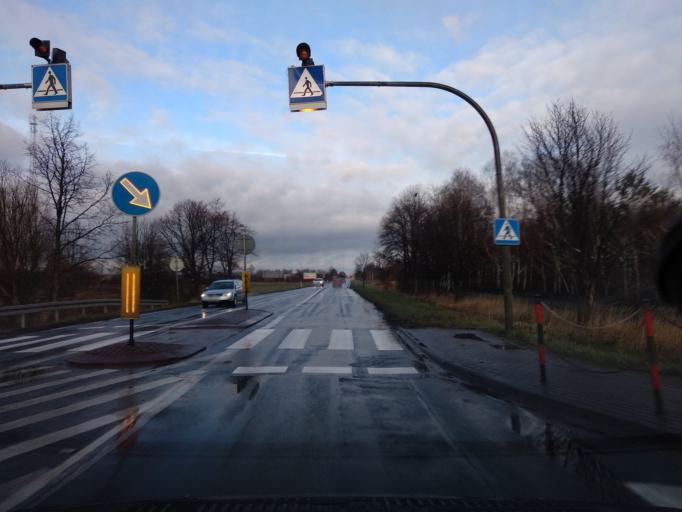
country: PL
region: Greater Poland Voivodeship
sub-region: Powiat koninski
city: Rychwal
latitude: 52.0731
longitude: 18.1582
